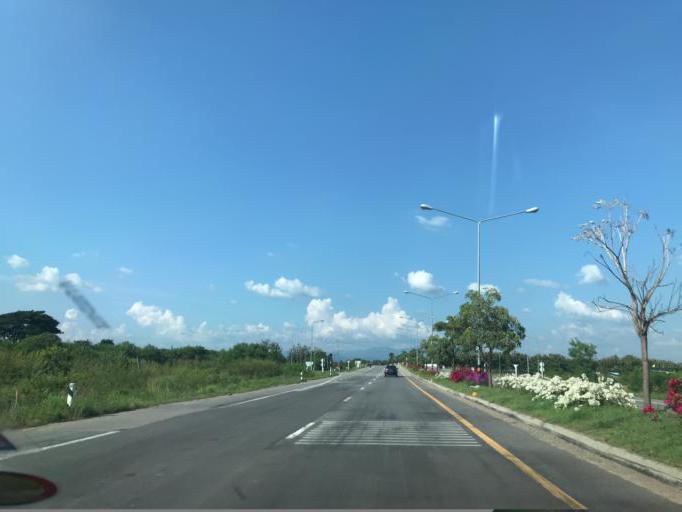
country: TH
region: Chiang Mai
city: San Pa Tong
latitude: 18.5607
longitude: 98.8499
